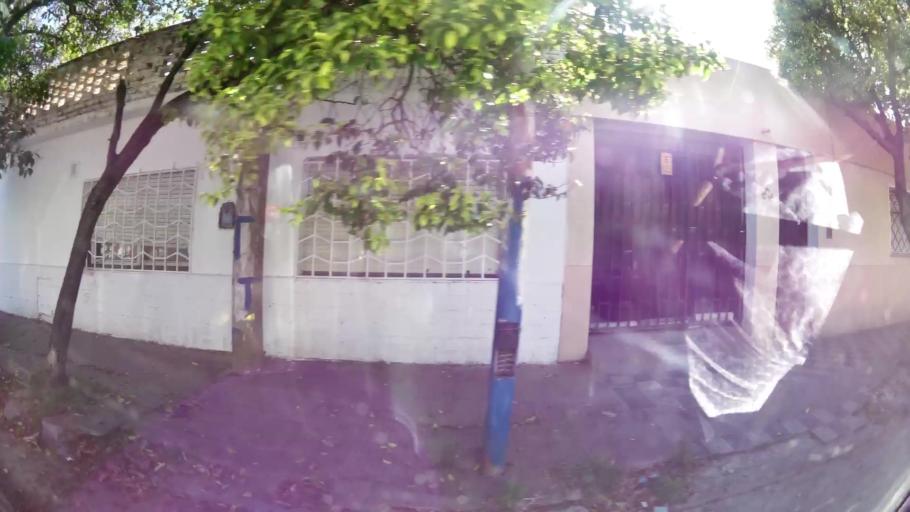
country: AR
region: Cordoba
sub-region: Departamento de Capital
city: Cordoba
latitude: -31.4389
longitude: -64.1537
